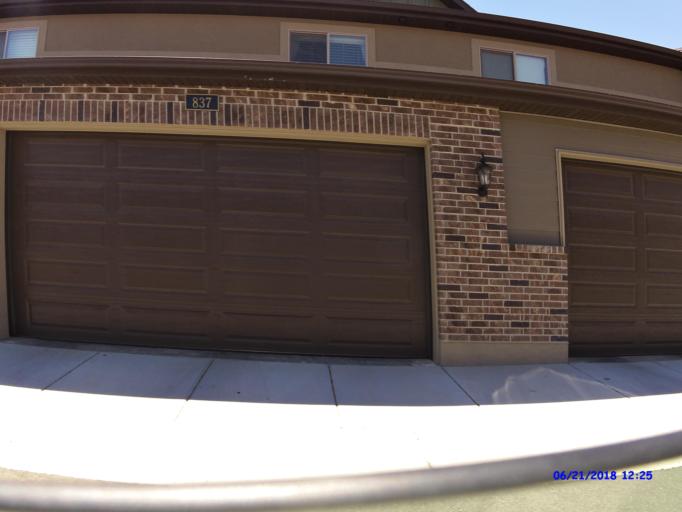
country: US
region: Utah
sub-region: Weber County
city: Harrisville
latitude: 41.2841
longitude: -111.9989
